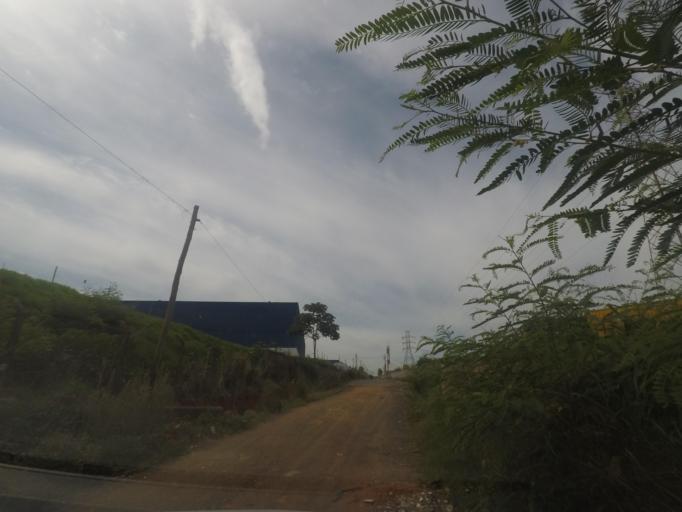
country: BR
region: Sao Paulo
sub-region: Sumare
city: Sumare
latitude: -22.8035
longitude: -47.2563
